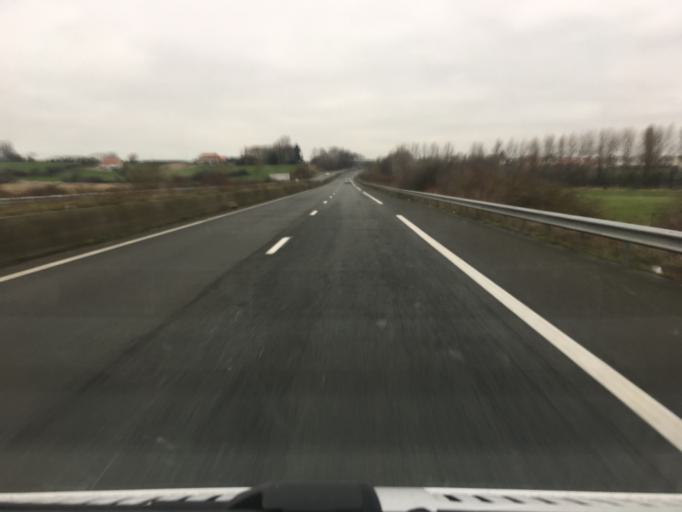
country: FR
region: Nord-Pas-de-Calais
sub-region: Departement du Pas-de-Calais
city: Marquise
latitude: 50.8104
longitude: 1.6945
